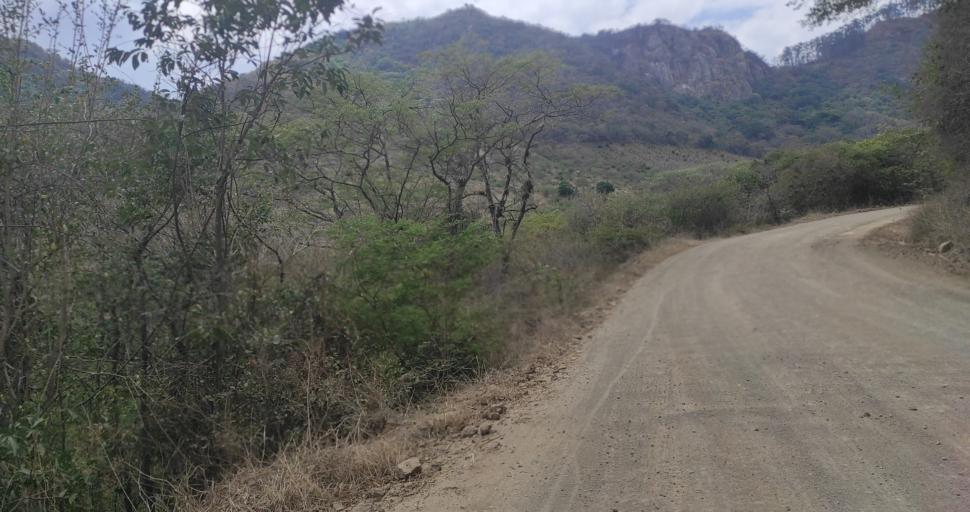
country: EC
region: Loja
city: Catacocha
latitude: -4.0272
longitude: -79.6417
